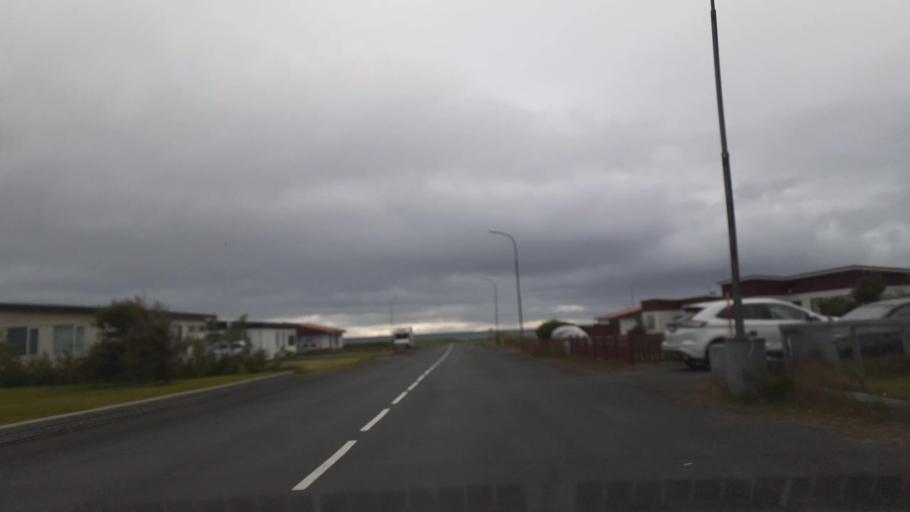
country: IS
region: Northeast
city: Husavik
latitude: 66.3026
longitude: -16.4465
